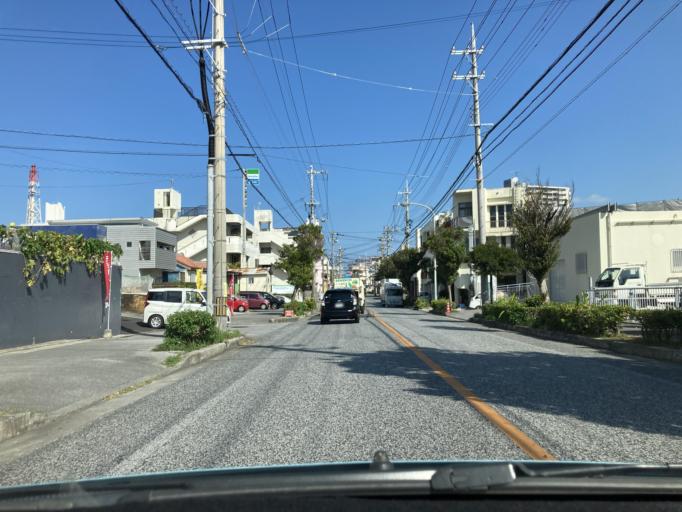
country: JP
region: Okinawa
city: Ginowan
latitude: 26.2635
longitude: 127.7242
